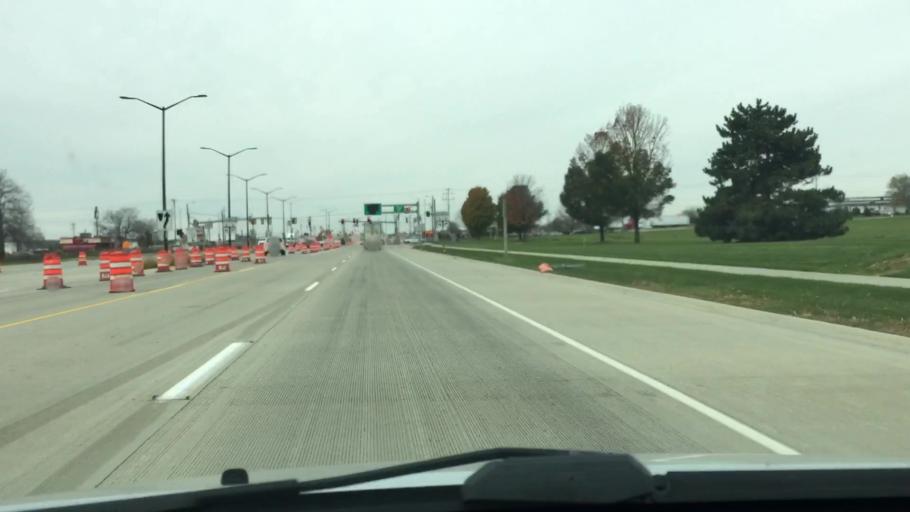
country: US
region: Wisconsin
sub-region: Racine County
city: Caledonia
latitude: 42.8725
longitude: -87.9298
